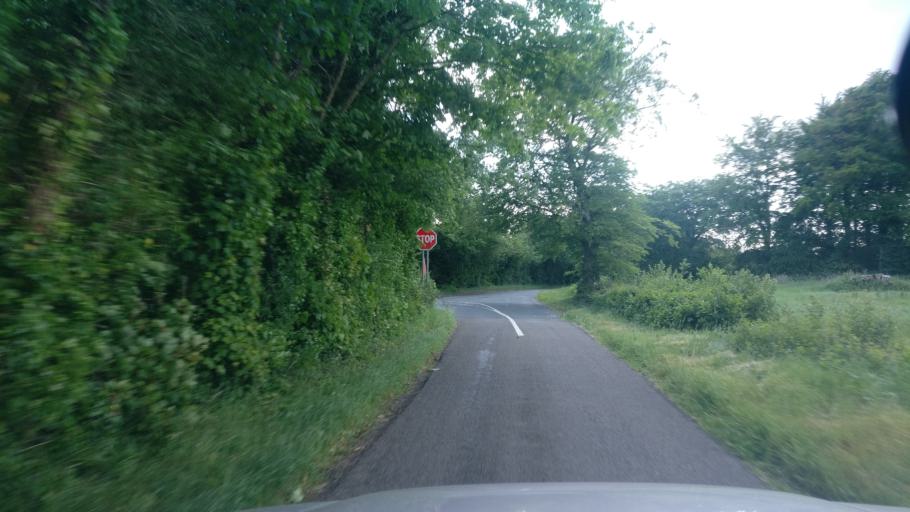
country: IE
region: Connaught
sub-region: County Galway
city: Ballinasloe
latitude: 53.2243
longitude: -8.2030
